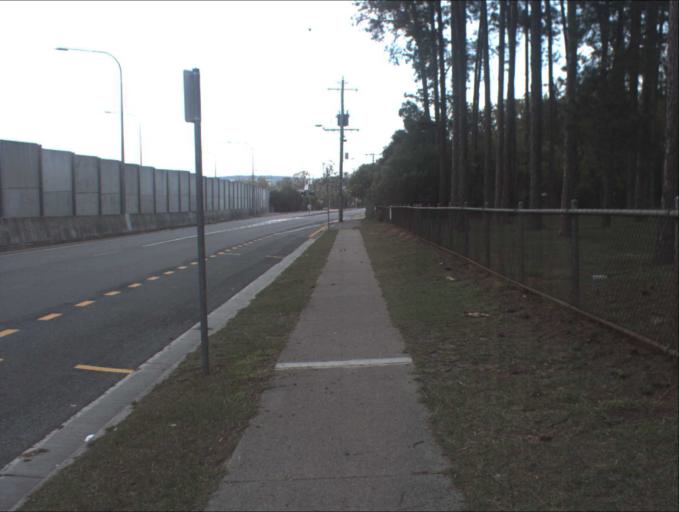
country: AU
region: Queensland
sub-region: Logan
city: Park Ridge South
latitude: -27.7024
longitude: 153.0388
